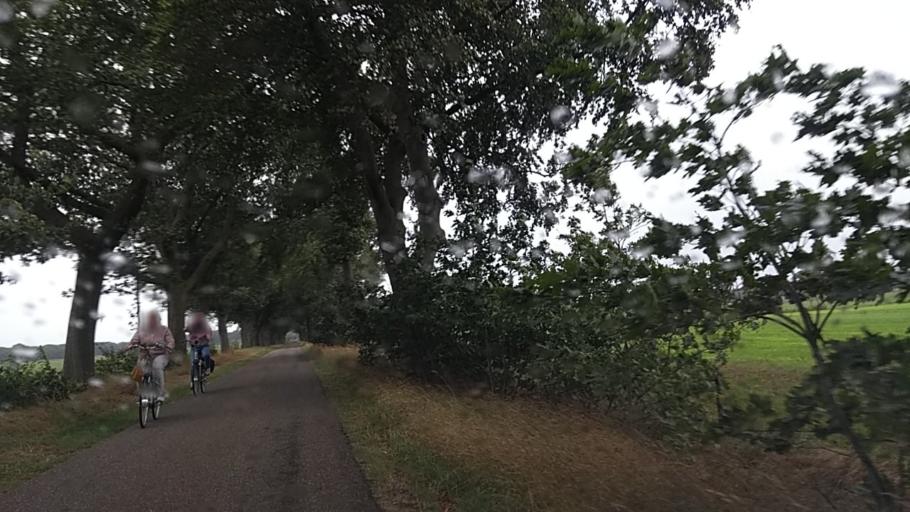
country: NL
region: Limburg
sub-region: Gemeente Leudal
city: Heythuysen
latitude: 51.3028
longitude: 5.8502
